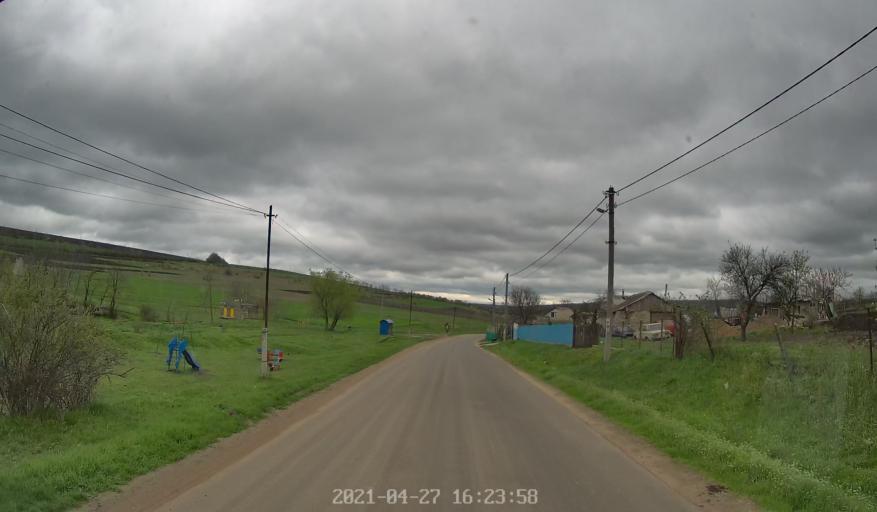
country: MD
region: Chisinau
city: Singera
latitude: 46.9953
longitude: 29.0199
